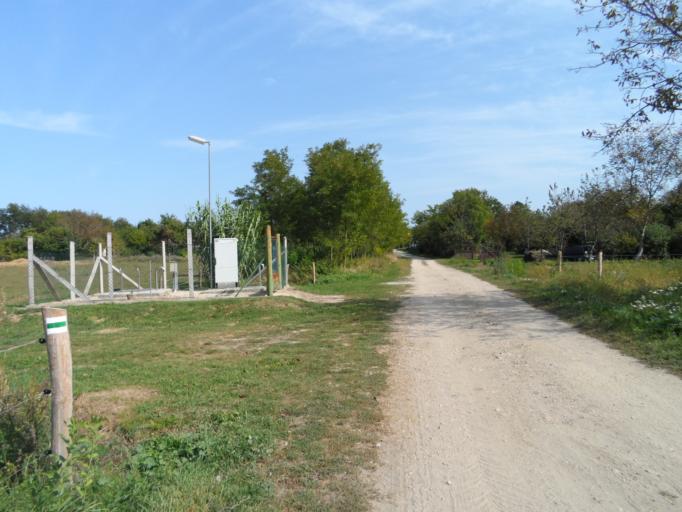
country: HU
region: Veszprem
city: Devecser
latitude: 47.1804
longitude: 17.4519
